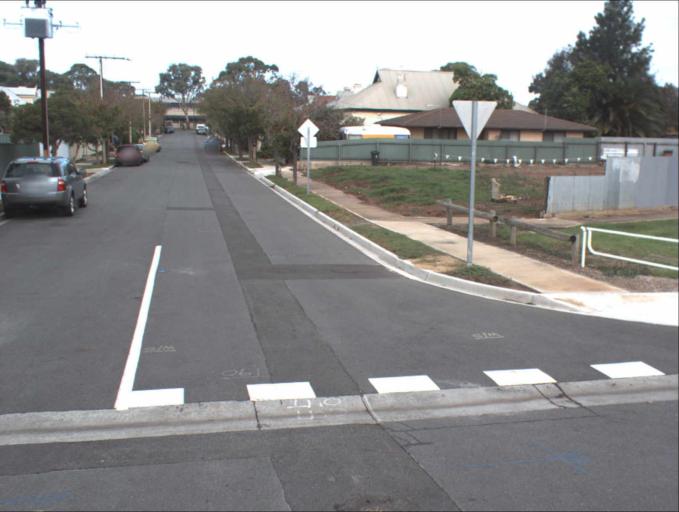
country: AU
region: South Australia
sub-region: Port Adelaide Enfield
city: Birkenhead
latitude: -34.8432
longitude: 138.4864
